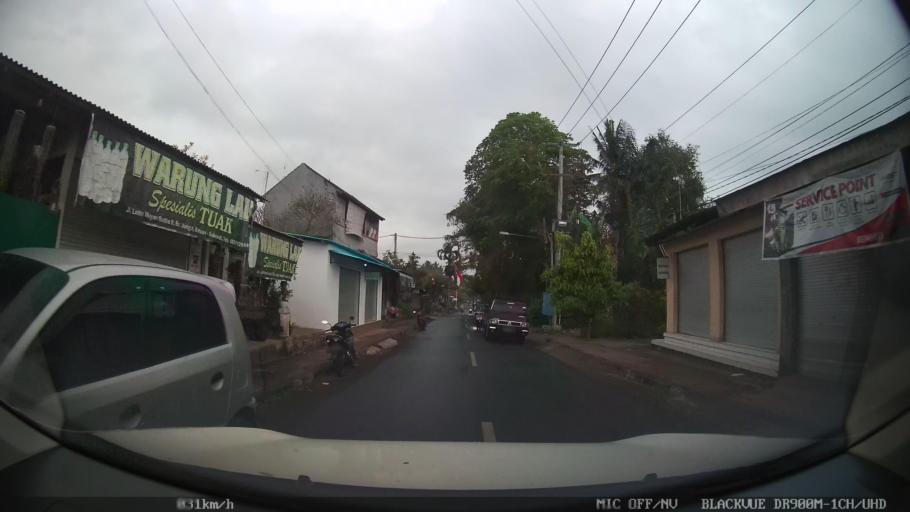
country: ID
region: Bali
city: Banjar Desa
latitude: -8.5887
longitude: 115.2796
